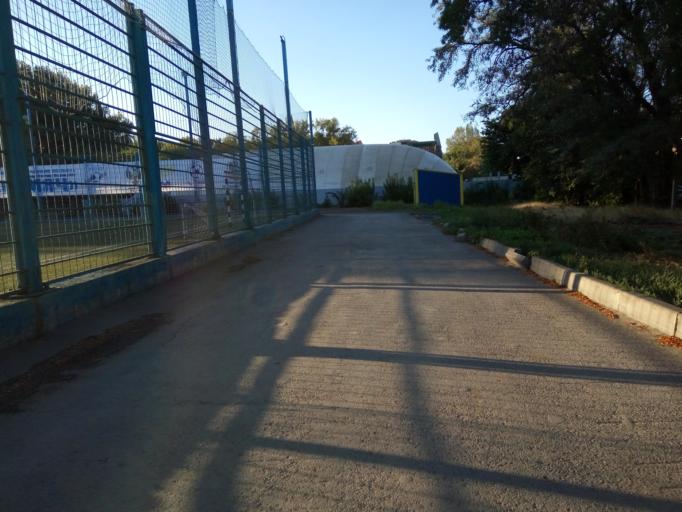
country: RU
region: Rostov
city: Rostov-na-Donu
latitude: 47.2442
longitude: 39.7585
